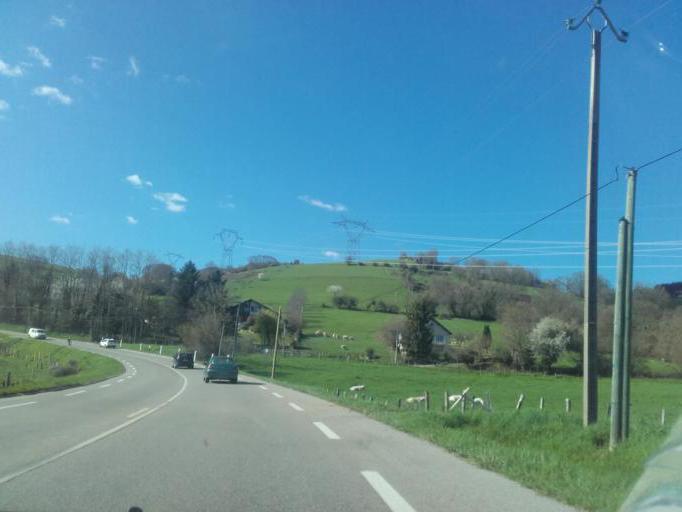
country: FR
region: Rhone-Alpes
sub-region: Departement de l'Isere
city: Saint-Hilaire-de-la-Cote
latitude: 45.3986
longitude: 5.3574
